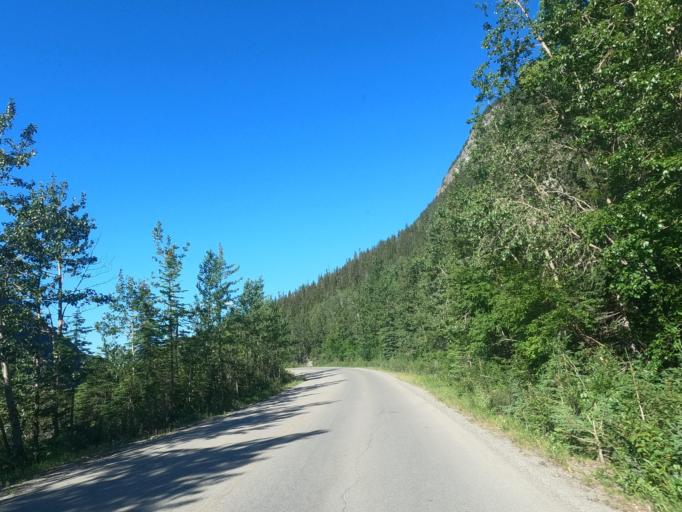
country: CA
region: Alberta
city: Lake Louise
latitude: 51.4193
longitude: -116.4478
